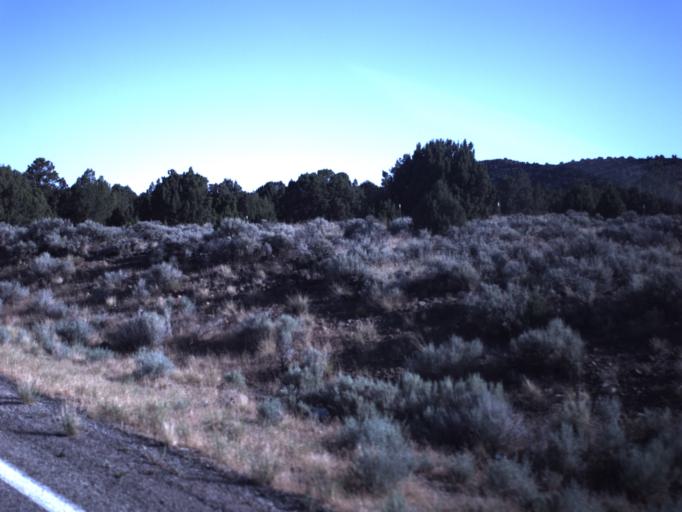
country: US
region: Utah
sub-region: Beaver County
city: Milford
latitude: 38.1229
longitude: -112.9518
